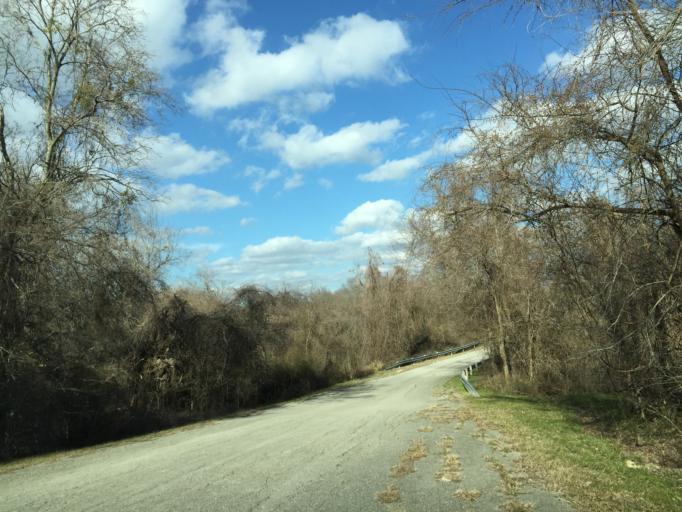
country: US
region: Texas
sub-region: Williamson County
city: Granger
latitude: 30.6723
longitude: -97.3646
